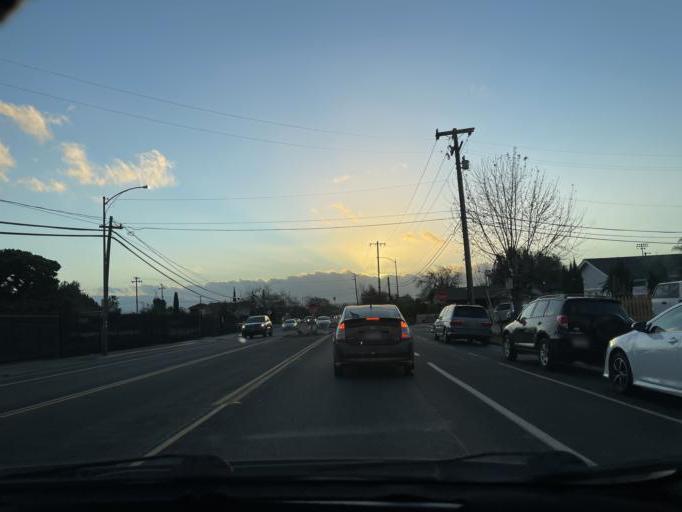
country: US
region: California
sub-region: Santa Clara County
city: Alum Rock
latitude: 37.3484
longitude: -121.8012
